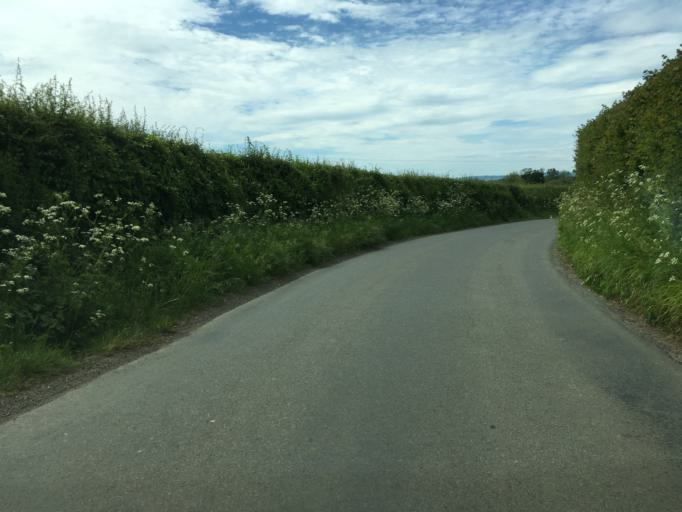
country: GB
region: England
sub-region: South Gloucestershire
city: Charfield
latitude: 51.6643
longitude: -2.3920
